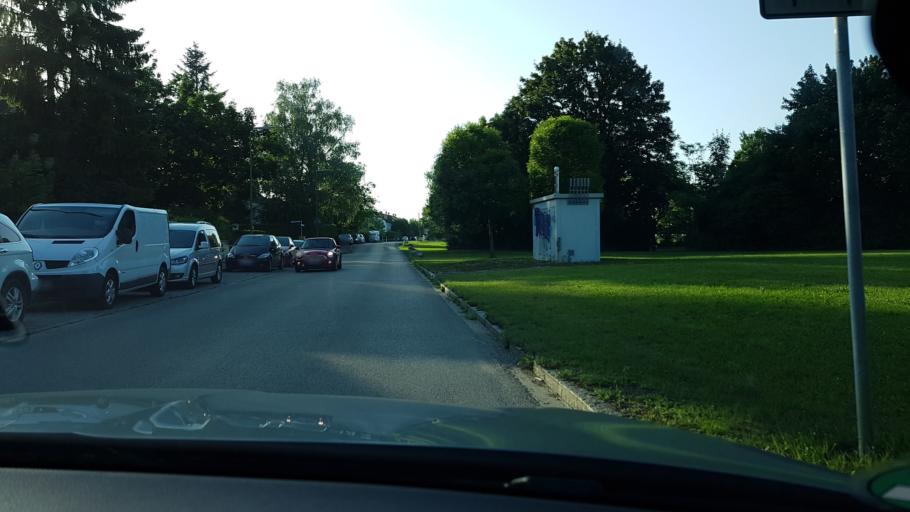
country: DE
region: Bavaria
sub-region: Upper Bavaria
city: Unterfoehring
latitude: 48.1570
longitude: 11.6537
